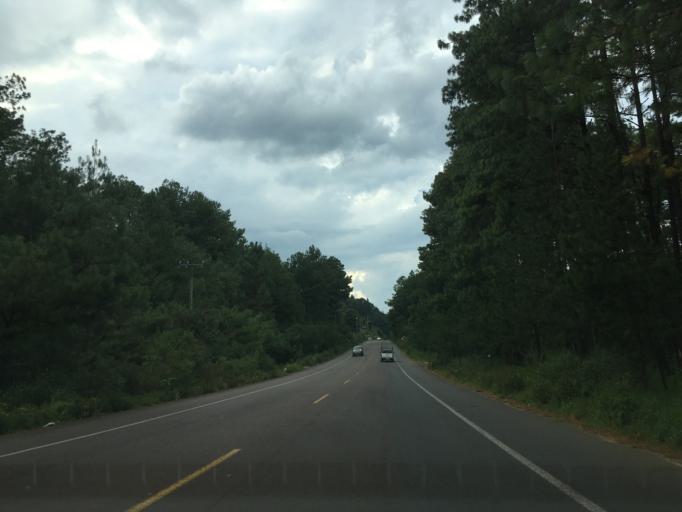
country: MX
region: Michoacan
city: Angahuan
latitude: 19.5258
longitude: -102.1877
